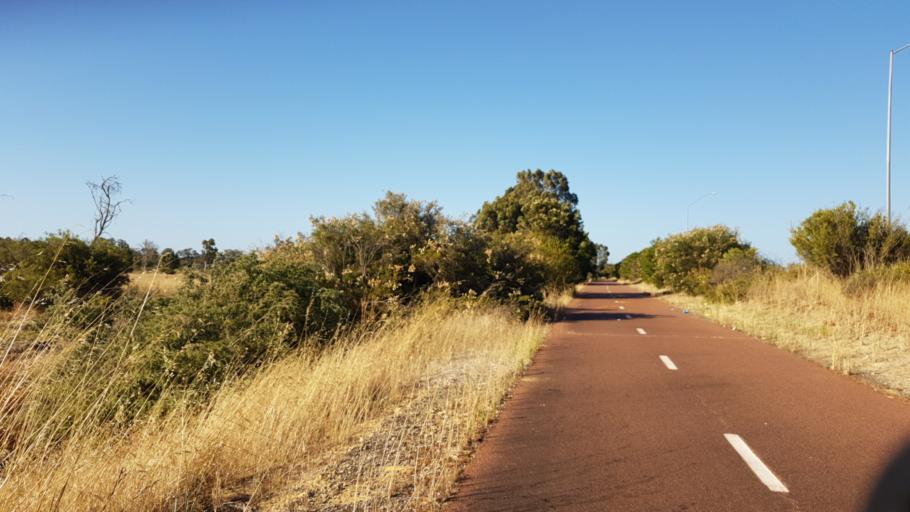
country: AU
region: Western Australia
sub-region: Kwinana
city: Wellard
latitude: -32.2793
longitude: 115.8393
